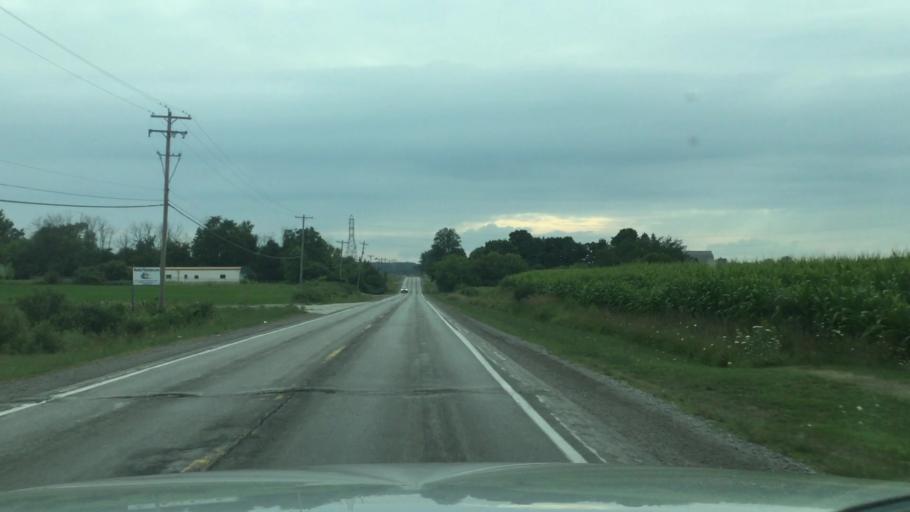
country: US
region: Michigan
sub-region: Saginaw County
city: Bridgeport
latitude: 43.3358
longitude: -83.8264
